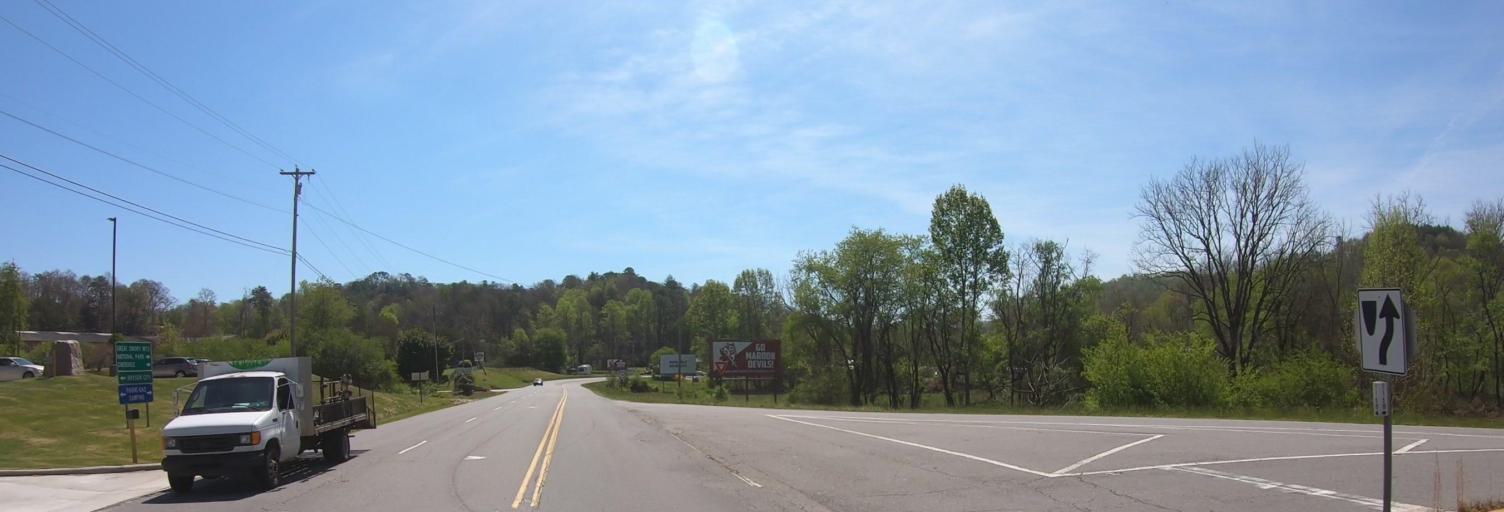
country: US
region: North Carolina
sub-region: Swain County
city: Bryson City
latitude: 35.4529
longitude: -83.3909
